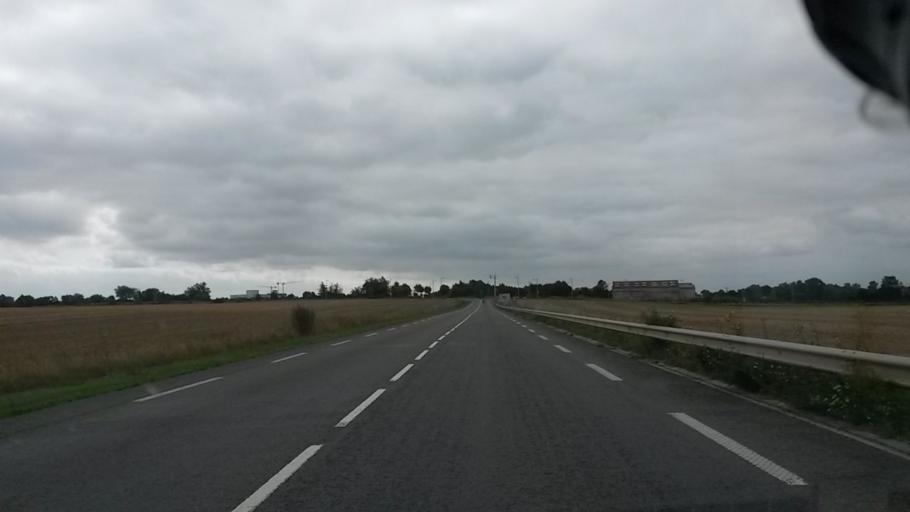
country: FR
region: Nord-Pas-de-Calais
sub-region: Departement du Pas-de-Calais
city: Bapaume
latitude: 50.1121
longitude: 2.8327
